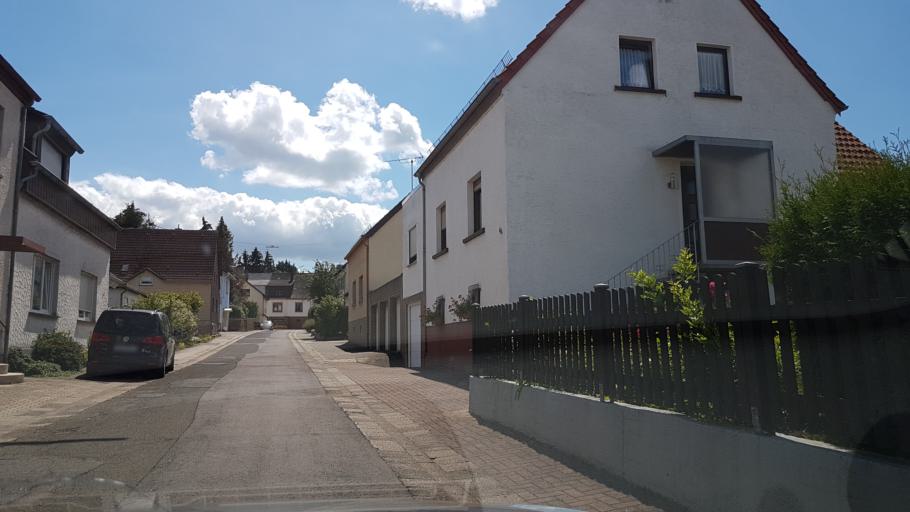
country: DE
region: Saarland
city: Illingen
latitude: 49.3720
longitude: 7.0602
